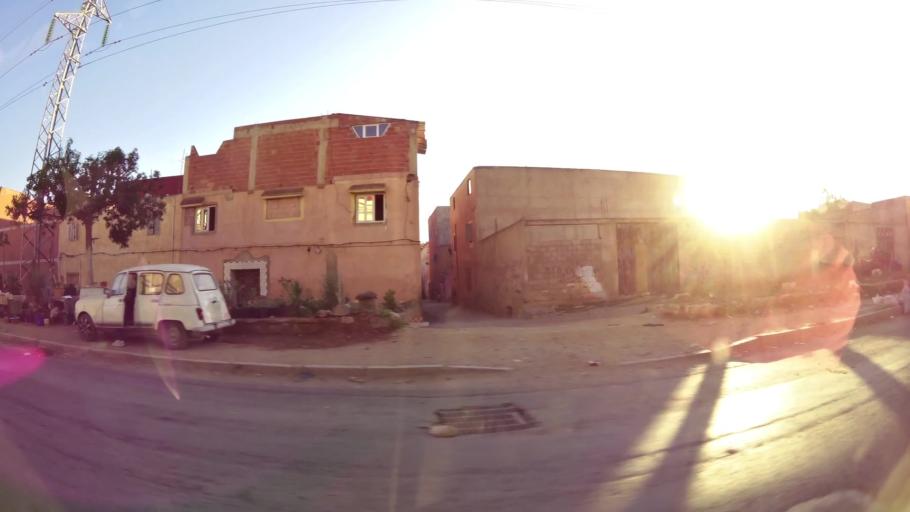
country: MA
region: Oriental
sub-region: Berkane-Taourirt
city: Berkane
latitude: 34.9236
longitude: -2.3126
